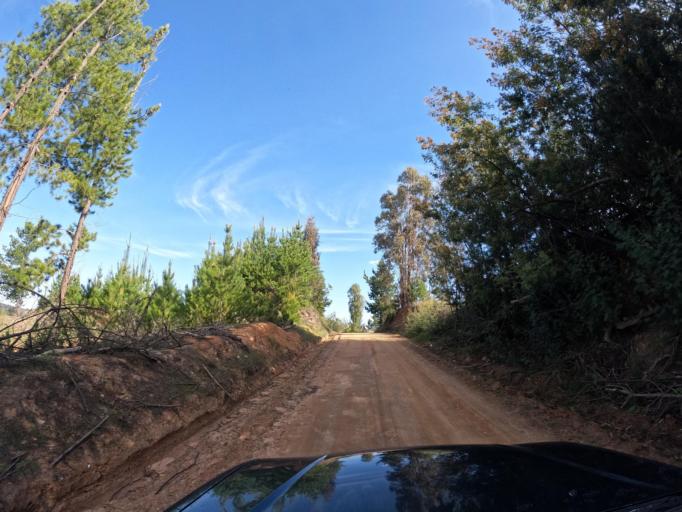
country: CL
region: Biobio
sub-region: Provincia de Biobio
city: La Laja
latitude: -37.1238
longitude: -72.7358
